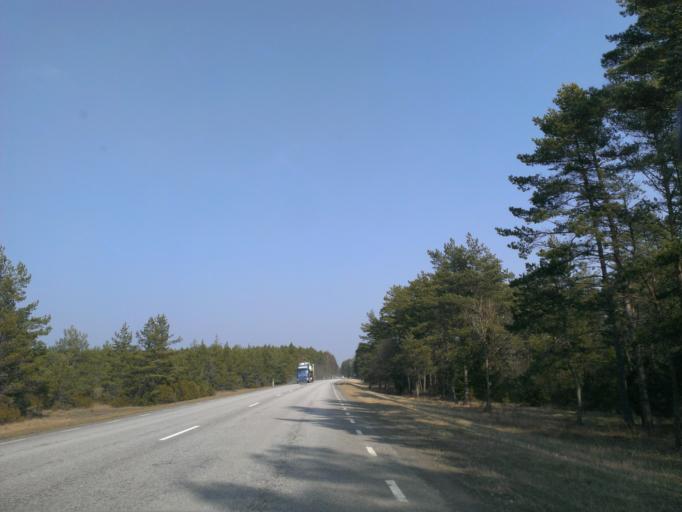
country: EE
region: Saare
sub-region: Kuressaare linn
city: Kuressaare
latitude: 58.3882
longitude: 22.7436
